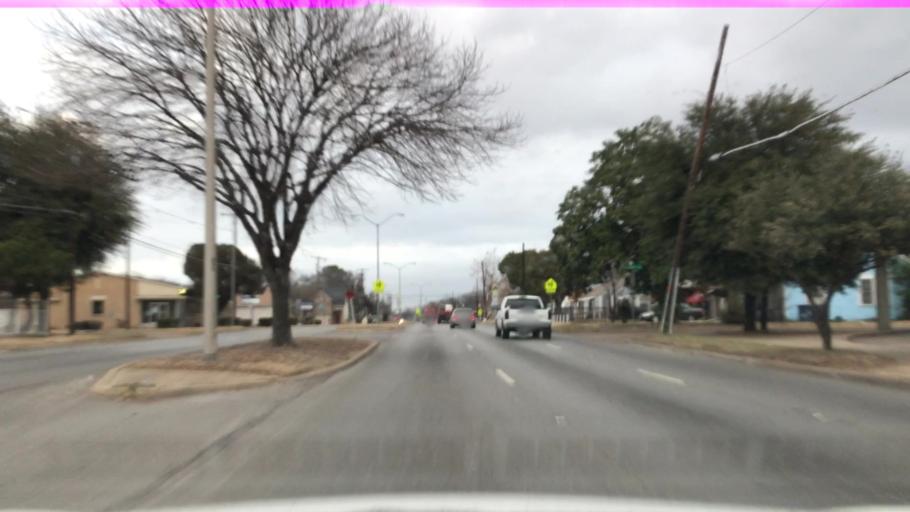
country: US
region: Texas
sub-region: Dallas County
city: Dallas
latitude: 32.7594
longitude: -96.7488
